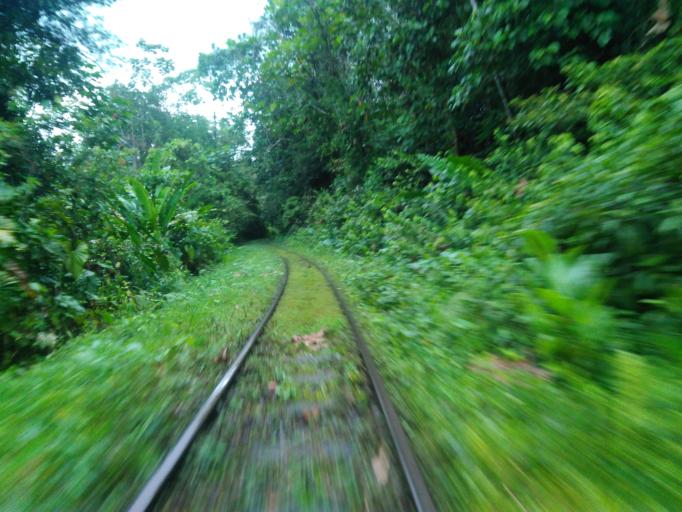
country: CO
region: Valle del Cauca
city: Buenaventura
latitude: 3.8429
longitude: -76.8761
